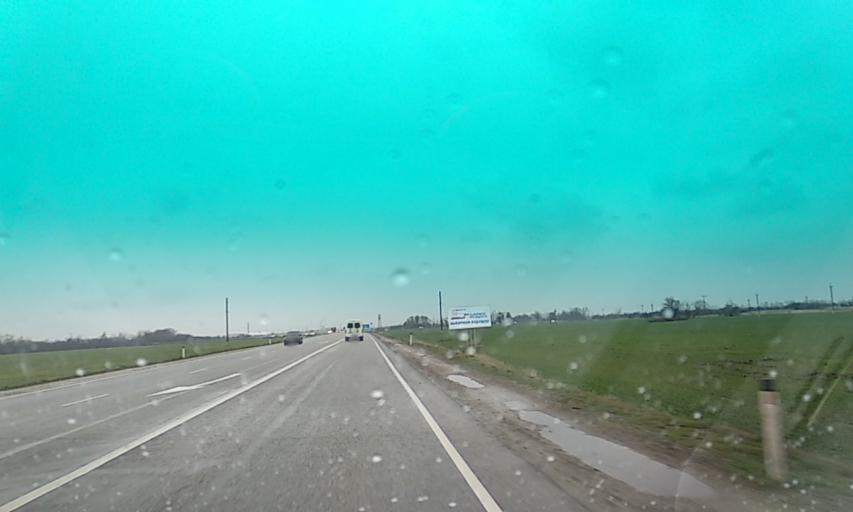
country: RU
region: Krasnodarskiy
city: Belorechensk
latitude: 44.8201
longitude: 39.8498
